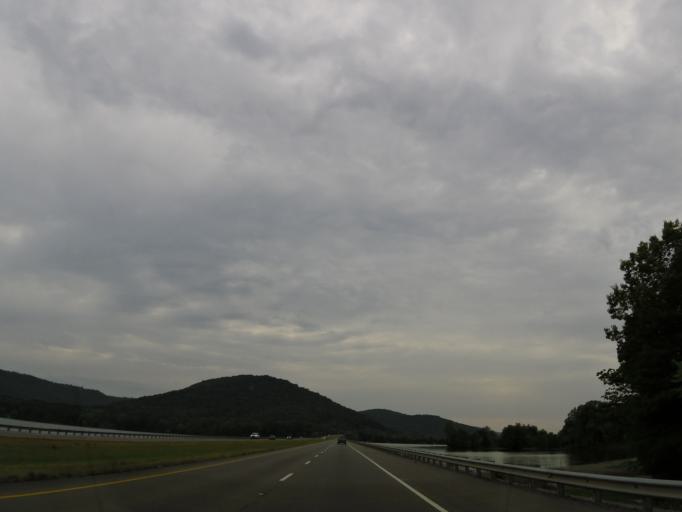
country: US
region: Alabama
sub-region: Jackson County
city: Scottsboro
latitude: 34.6200
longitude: -86.1040
